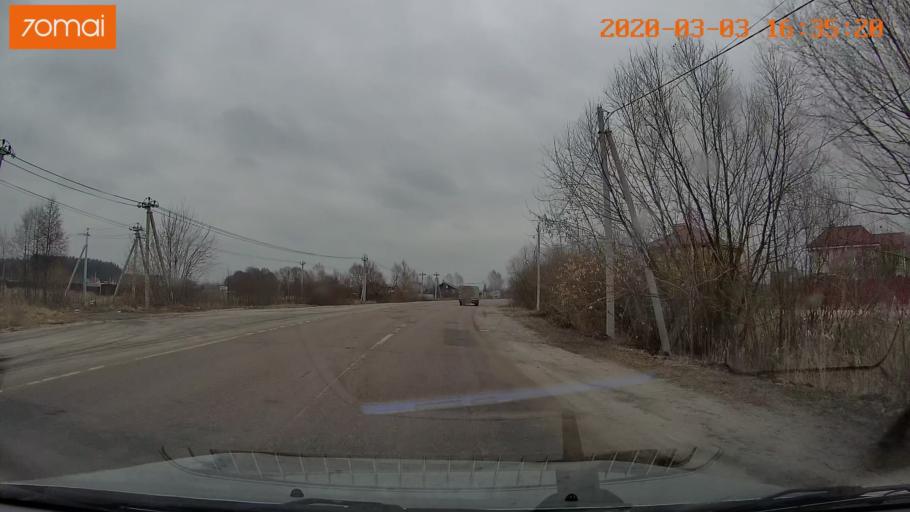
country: RU
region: Moskovskaya
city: Lopatinskiy
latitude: 55.4051
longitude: 38.7638
